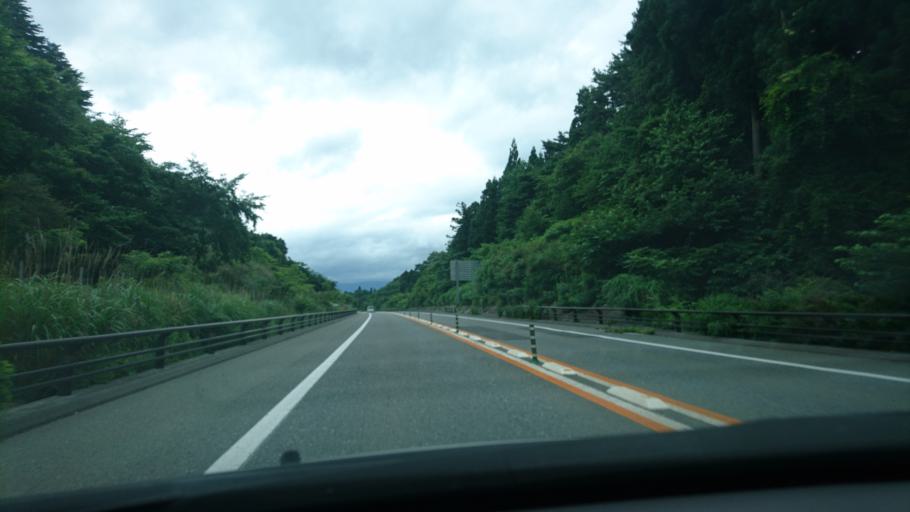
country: JP
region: Iwate
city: Ofunato
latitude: 39.0446
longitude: 141.7155
